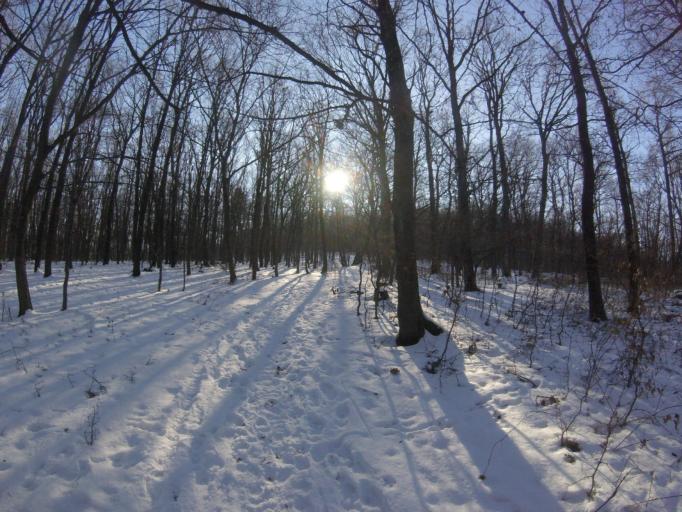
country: SK
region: Nitriansky
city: Sahy
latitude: 47.9891
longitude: 18.8884
